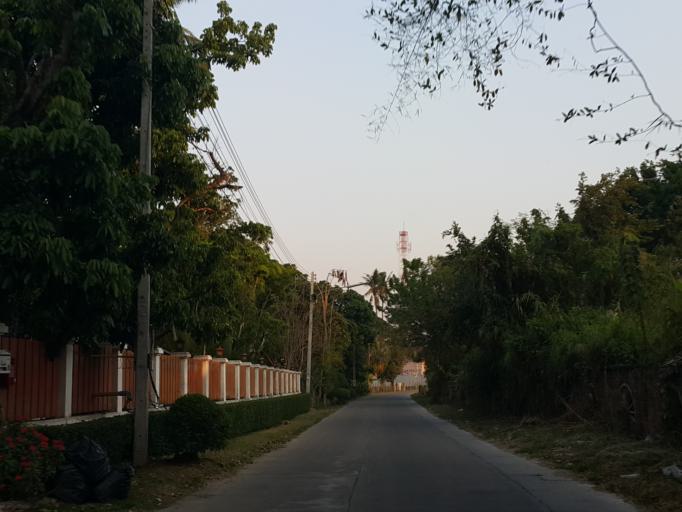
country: TH
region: Chiang Mai
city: San Sai
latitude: 18.8810
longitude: 98.9662
